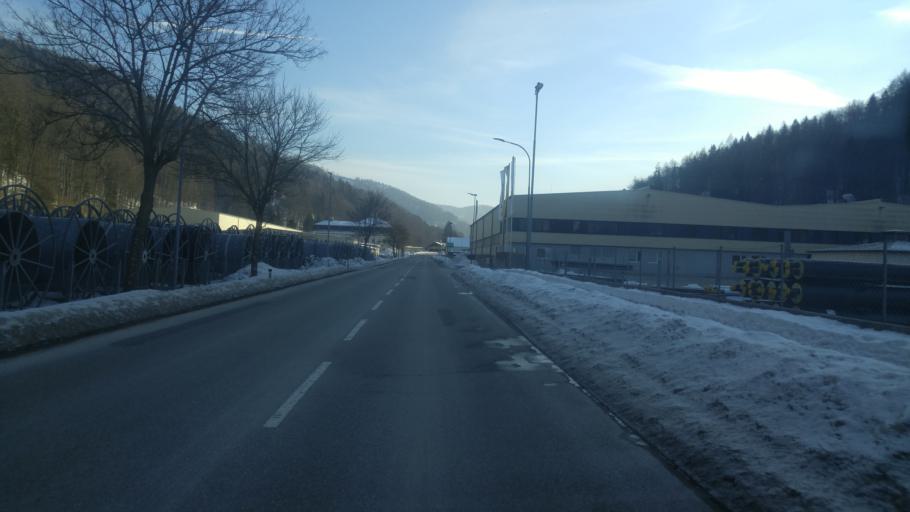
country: AT
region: Lower Austria
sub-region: Politischer Bezirk Lilienfeld
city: Hohenberg
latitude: 47.9254
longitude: 15.6126
